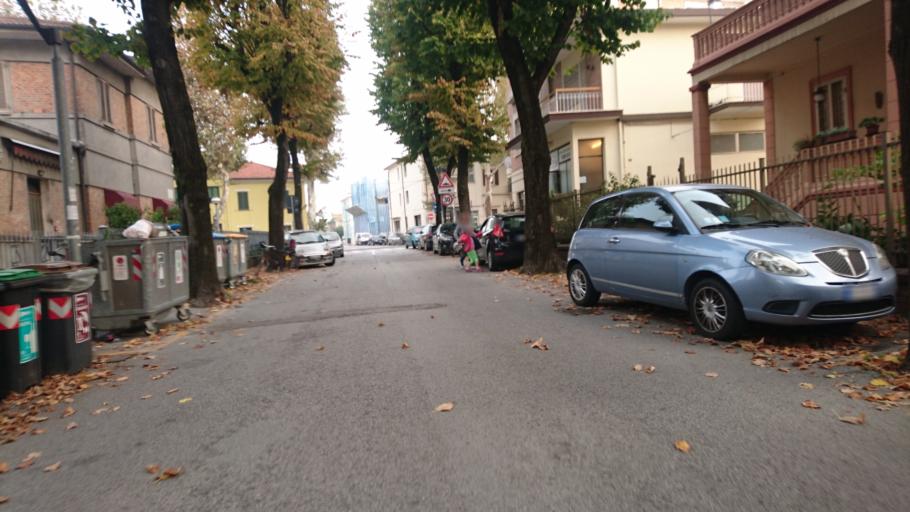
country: IT
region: Emilia-Romagna
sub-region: Provincia di Rimini
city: Rimini
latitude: 44.0566
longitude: 12.5755
